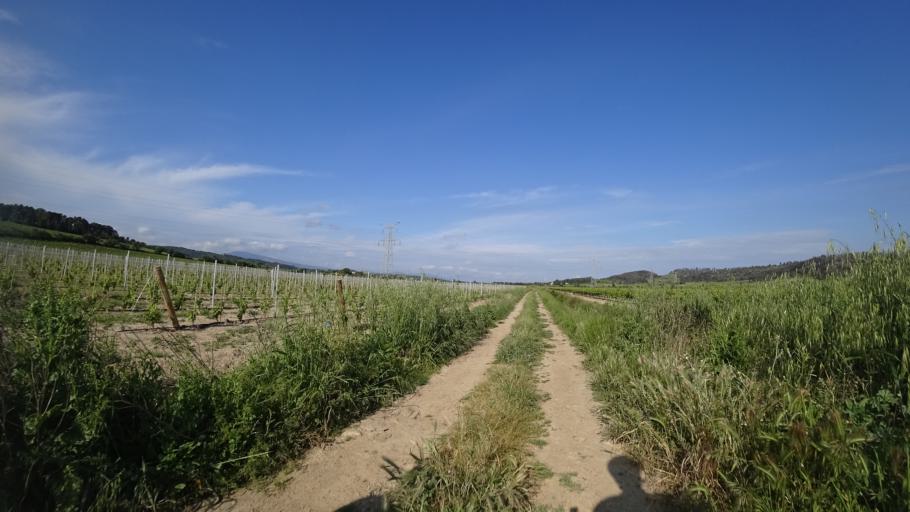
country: FR
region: Languedoc-Roussillon
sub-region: Departement de l'Herault
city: Olonzac
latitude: 43.2379
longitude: 2.7217
